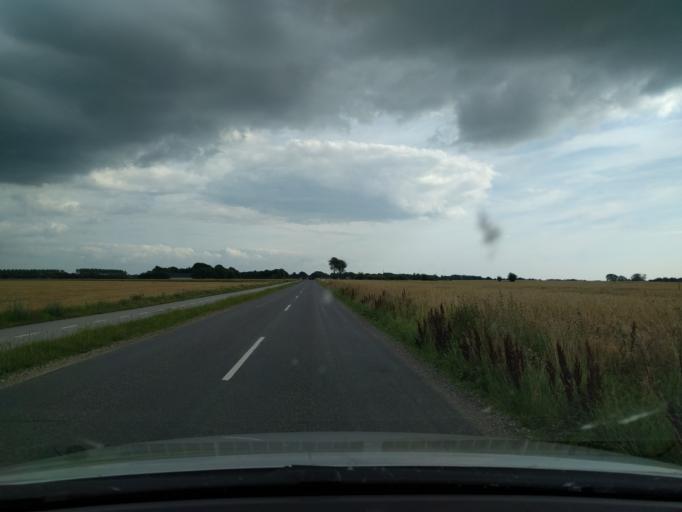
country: DK
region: Central Jutland
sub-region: Herning Kommune
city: Snejbjerg
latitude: 56.1002
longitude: 8.9098
